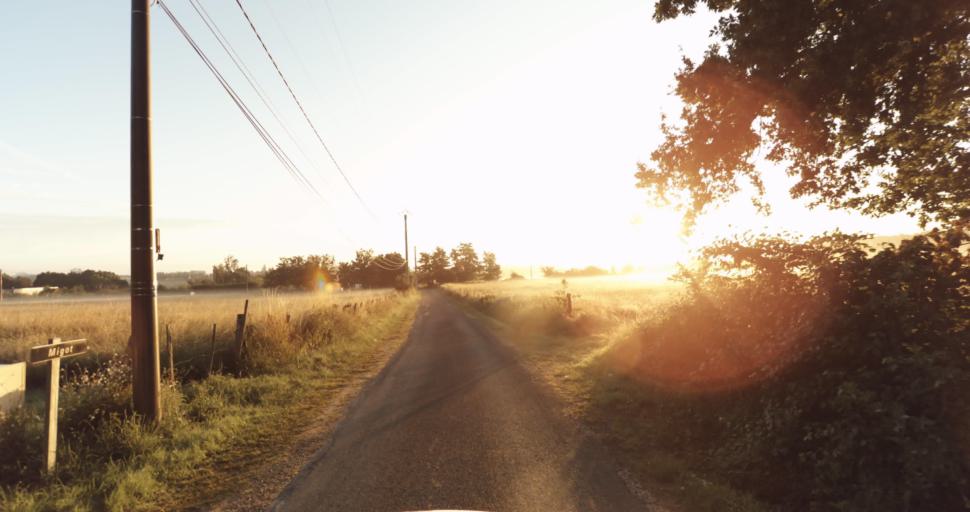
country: FR
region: Aquitaine
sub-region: Departement de la Gironde
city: Bazas
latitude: 44.4284
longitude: -0.1957
